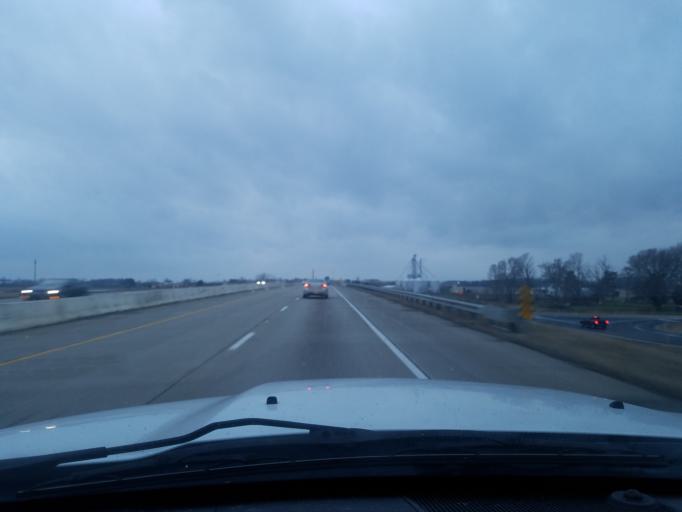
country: US
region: Indiana
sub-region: Huntington County
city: Roanoke
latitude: 40.9588
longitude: -85.2721
